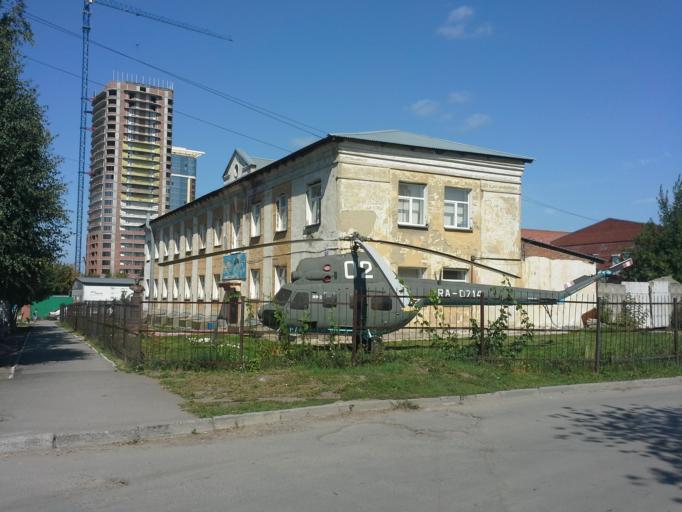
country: RU
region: Novosibirsk
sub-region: Novosibirskiy Rayon
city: Novosibirsk
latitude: 55.0505
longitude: 82.9274
